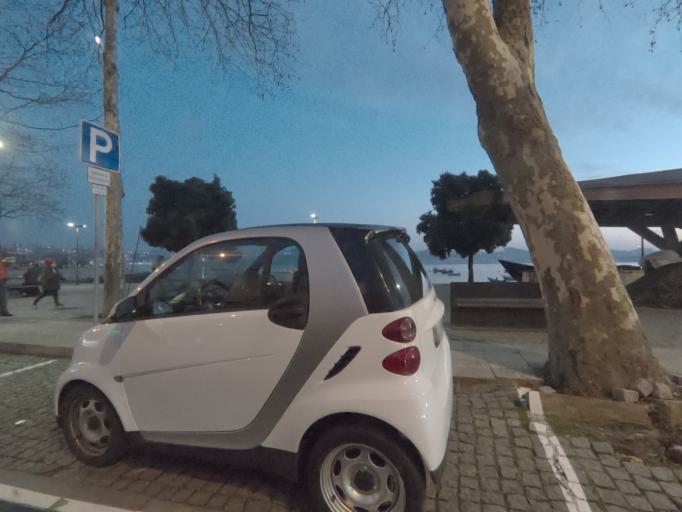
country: PT
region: Porto
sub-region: Vila Nova de Gaia
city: Canidelo
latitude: 41.1480
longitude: -8.6653
